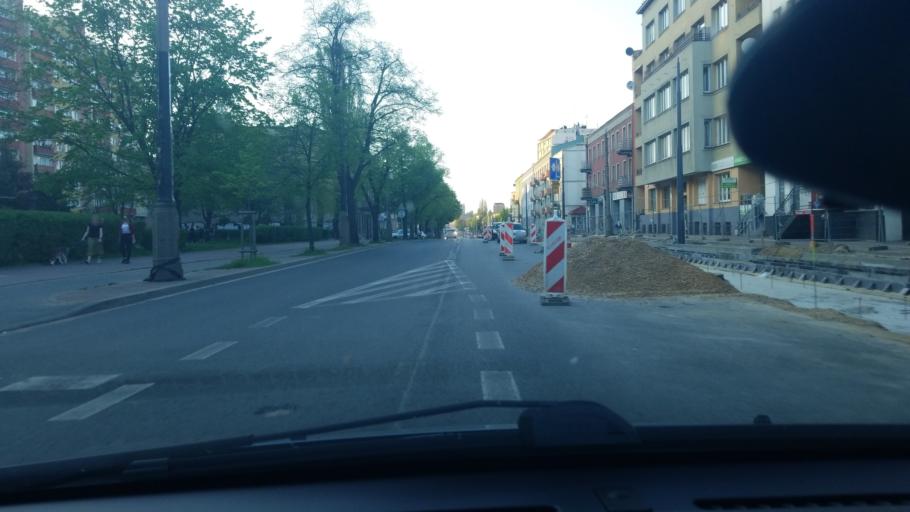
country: PL
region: Silesian Voivodeship
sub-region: Czestochowa
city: Czestochowa
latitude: 50.8139
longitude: 19.1183
